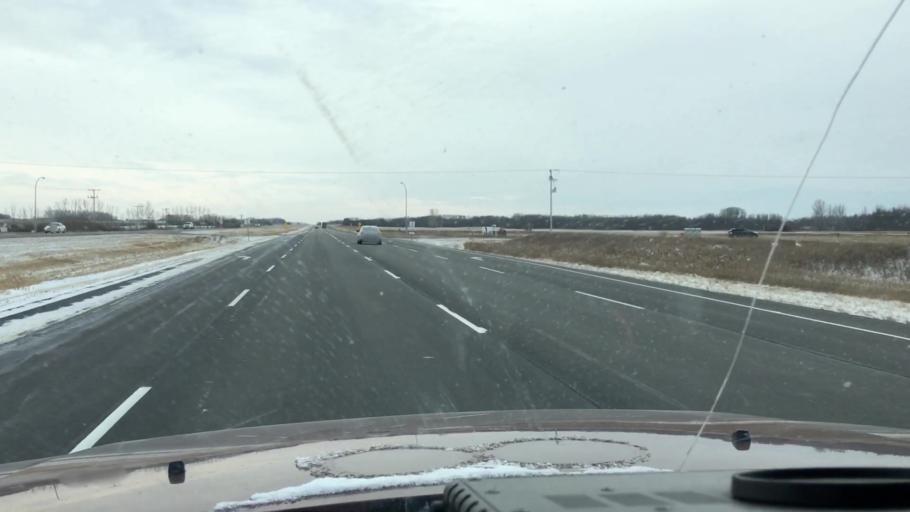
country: CA
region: Saskatchewan
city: Saskatoon
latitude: 51.9994
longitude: -106.5677
